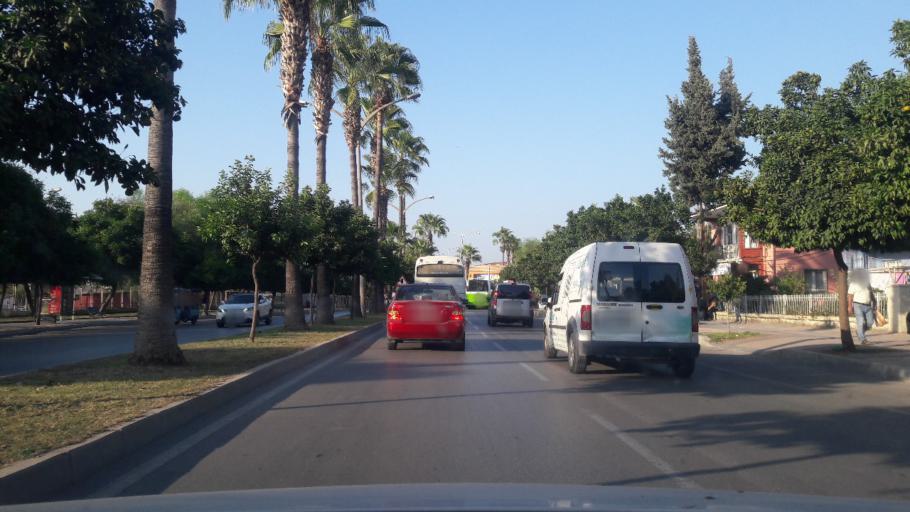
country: TR
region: Adana
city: Seyhan
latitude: 36.9914
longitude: 35.2989
